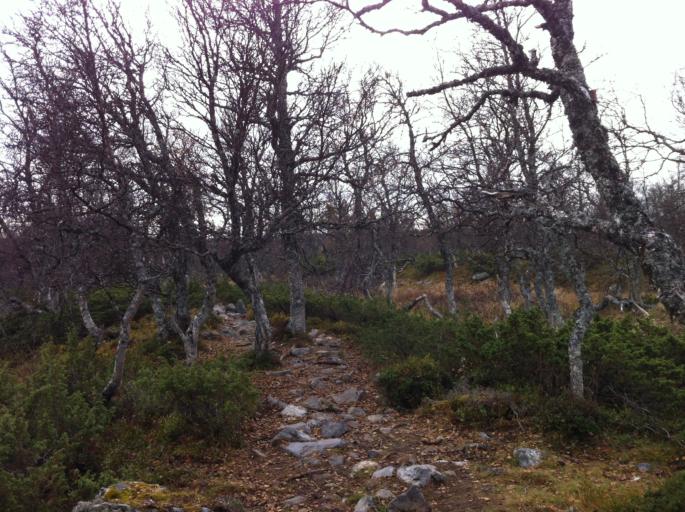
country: NO
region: Hedmark
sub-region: Engerdal
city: Engerdal
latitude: 62.0956
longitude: 12.2653
